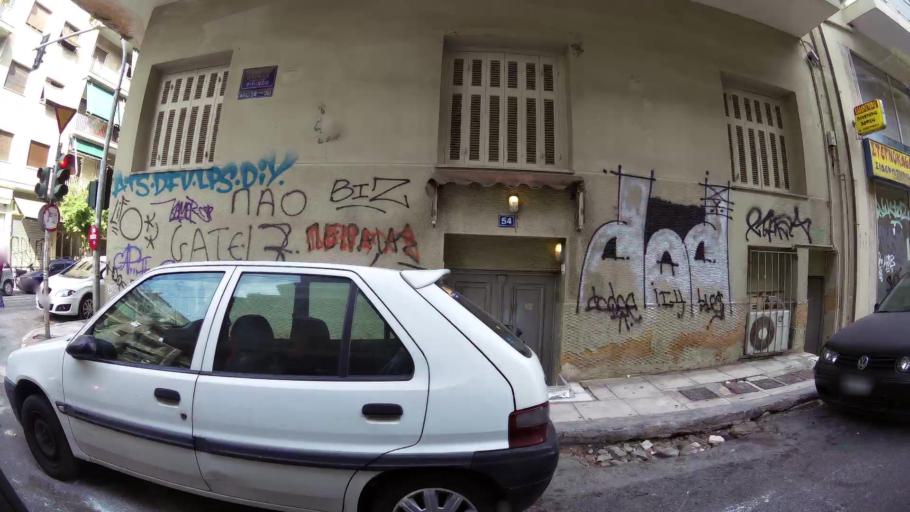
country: GR
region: Attica
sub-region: Nomarchia Athinas
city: Kipseli
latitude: 37.9972
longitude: 23.7301
